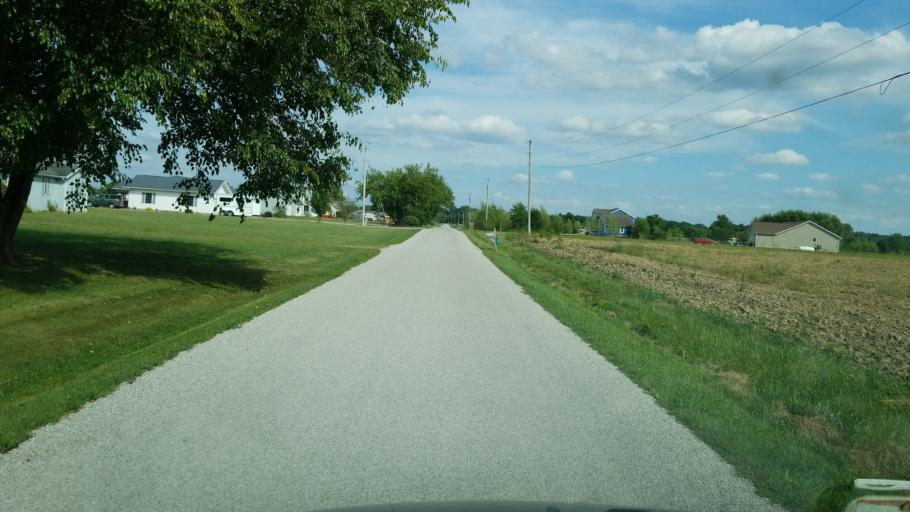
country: US
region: Ohio
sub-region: Delaware County
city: Ashley
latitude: 40.4368
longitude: -83.0100
